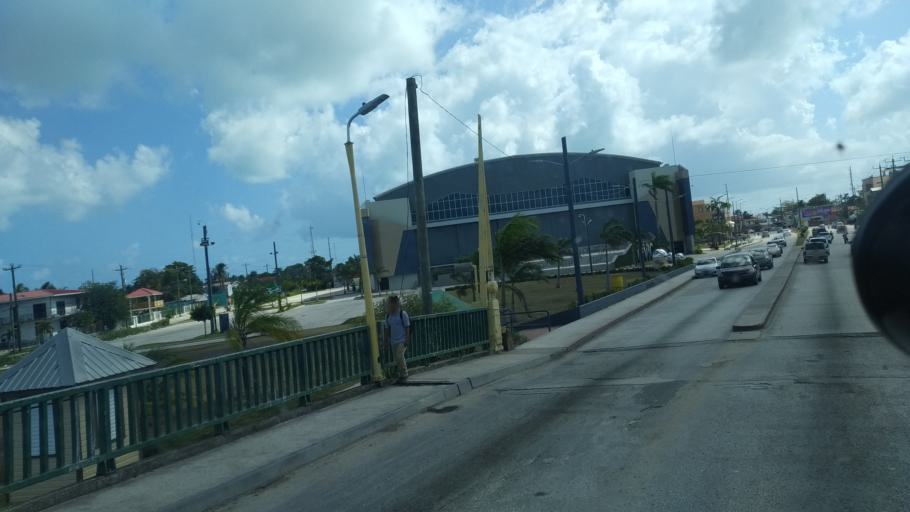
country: BZ
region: Belize
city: Belize City
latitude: 17.5027
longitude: -88.1974
